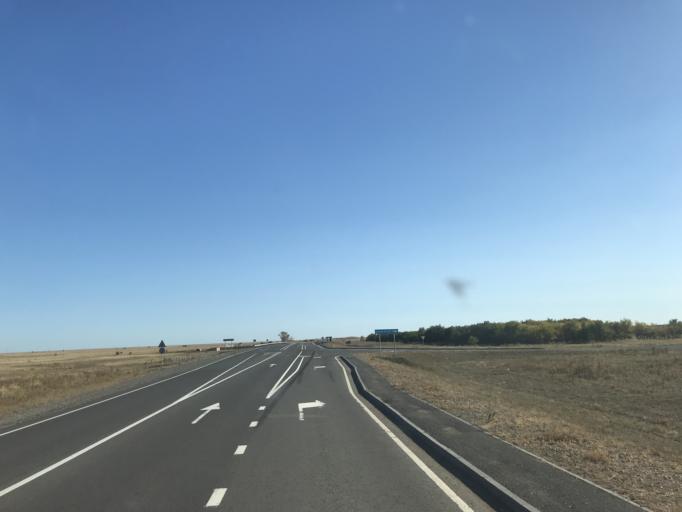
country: KZ
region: Pavlodar
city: Aksu
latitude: 52.0184
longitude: 77.2323
